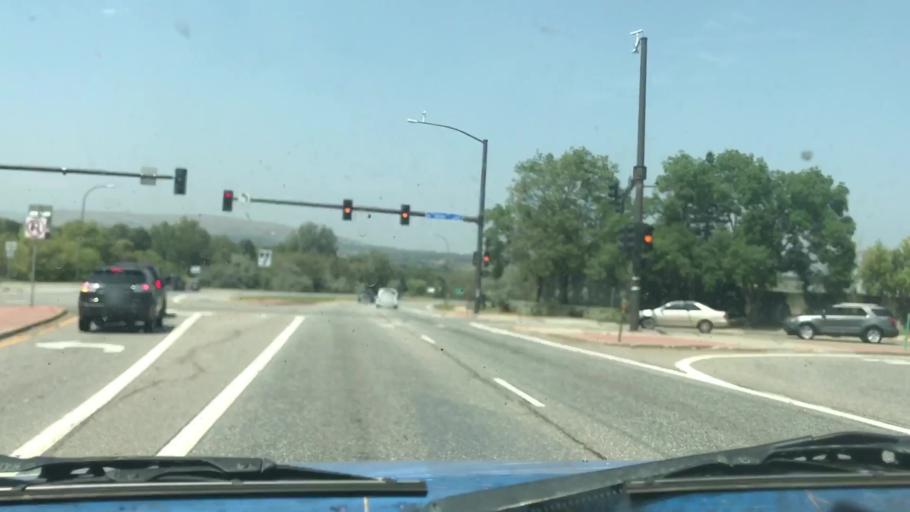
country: US
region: Colorado
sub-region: Jefferson County
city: Lakewood
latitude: 39.6559
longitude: -105.1105
